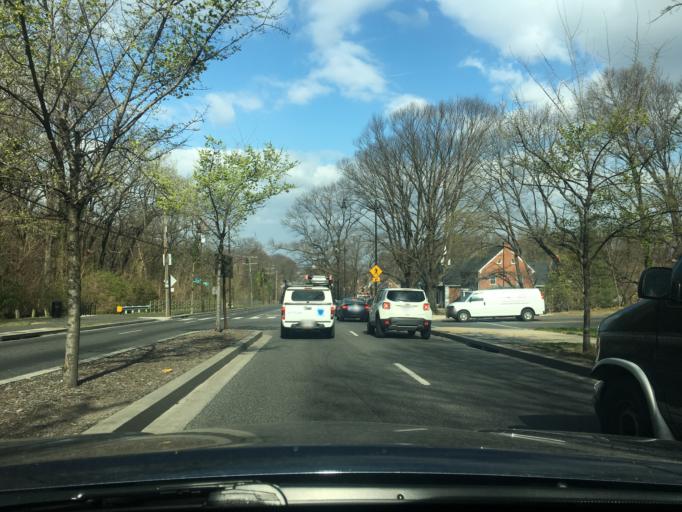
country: US
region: Maryland
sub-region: Prince George's County
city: Silver Hill
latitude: 38.8661
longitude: -76.9524
